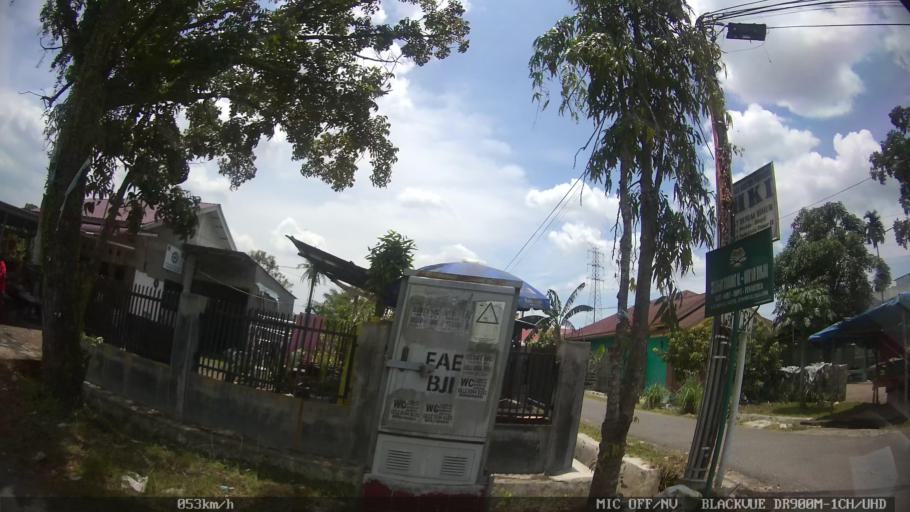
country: ID
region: North Sumatra
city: Binjai
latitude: 3.6278
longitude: 98.5178
